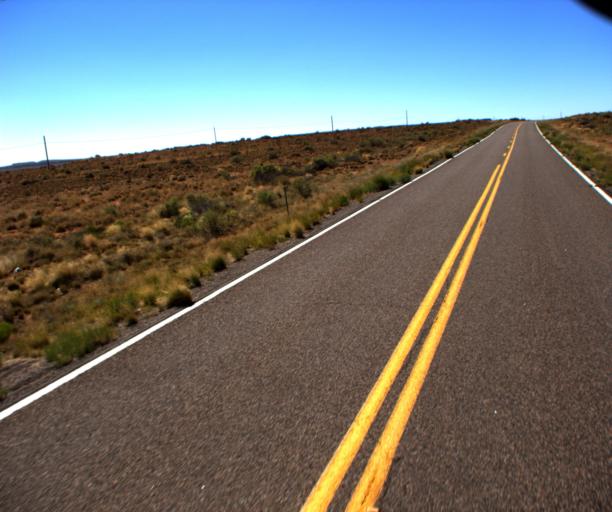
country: US
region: Arizona
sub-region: Coconino County
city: LeChee
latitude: 35.1089
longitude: -110.8662
